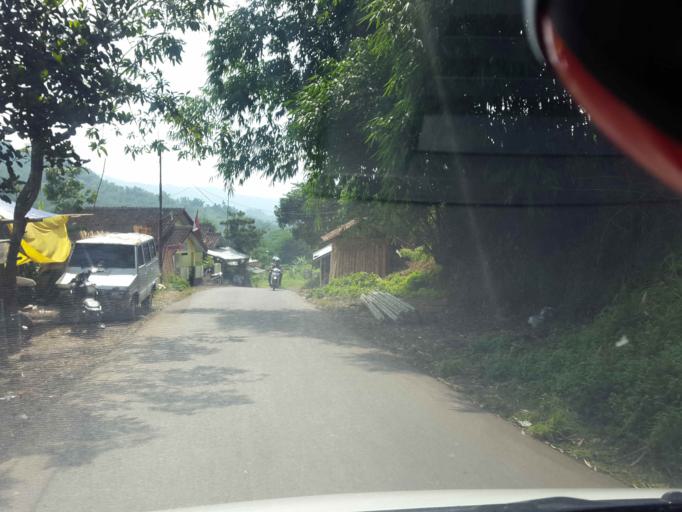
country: ID
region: West Java
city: Sukabumi
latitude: -6.9194
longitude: 107.0050
